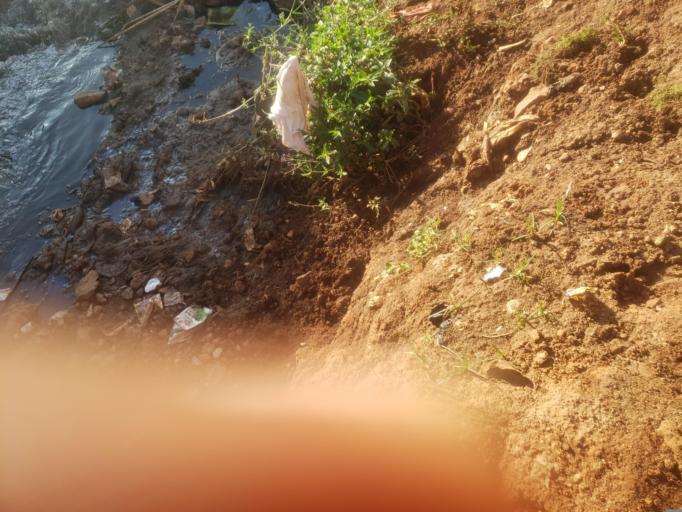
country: KE
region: Nairobi Area
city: Nairobi
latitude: -1.3125
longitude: 36.7732
